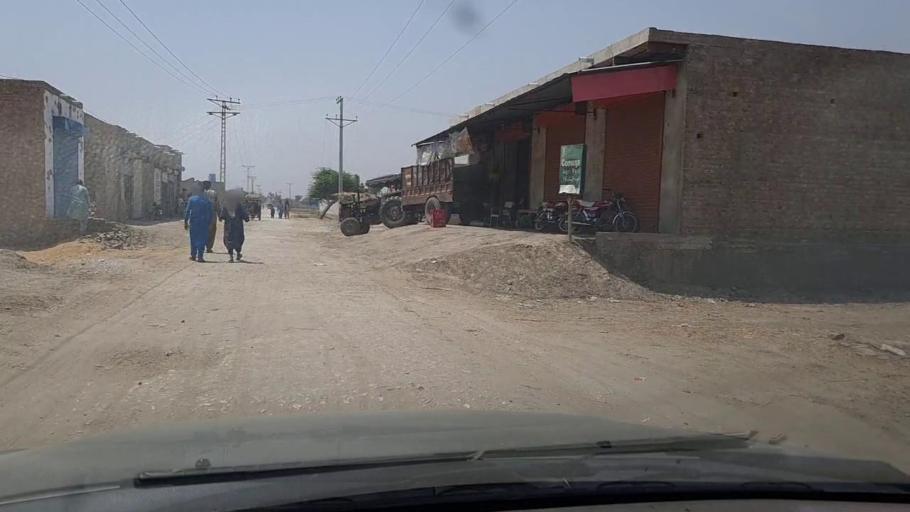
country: PK
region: Sindh
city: Miro Khan
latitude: 27.7617
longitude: 68.1066
